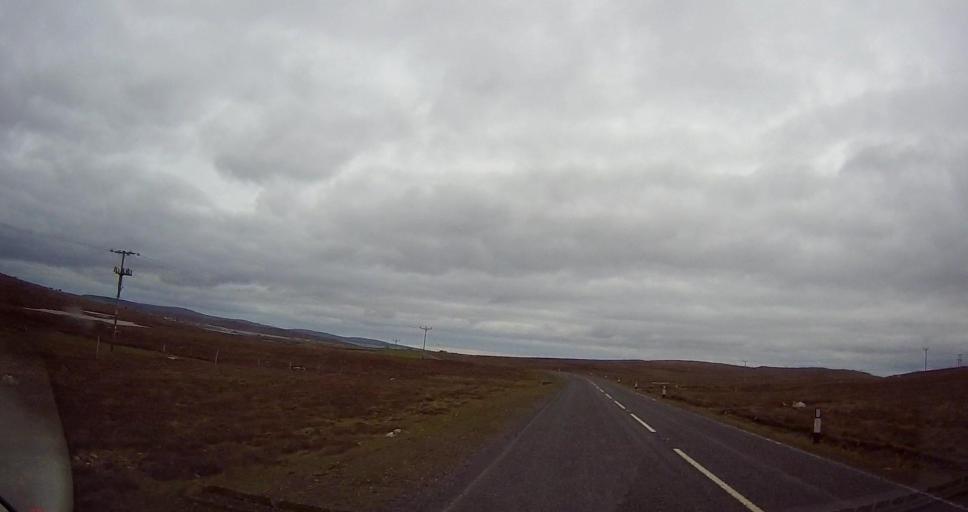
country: GB
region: Scotland
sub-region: Shetland Islands
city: Shetland
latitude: 60.7109
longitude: -0.9176
